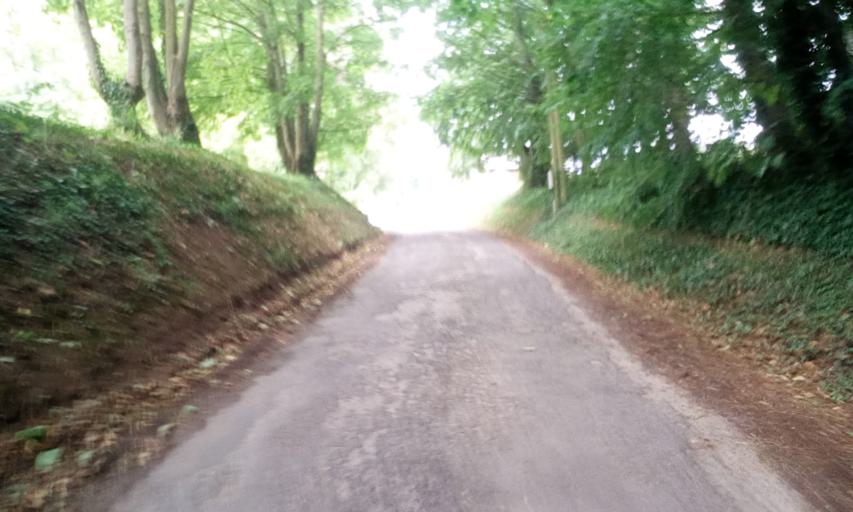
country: FR
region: Lower Normandy
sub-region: Departement du Calvados
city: Tilly-sur-Seulles
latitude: 49.2168
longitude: -0.6234
